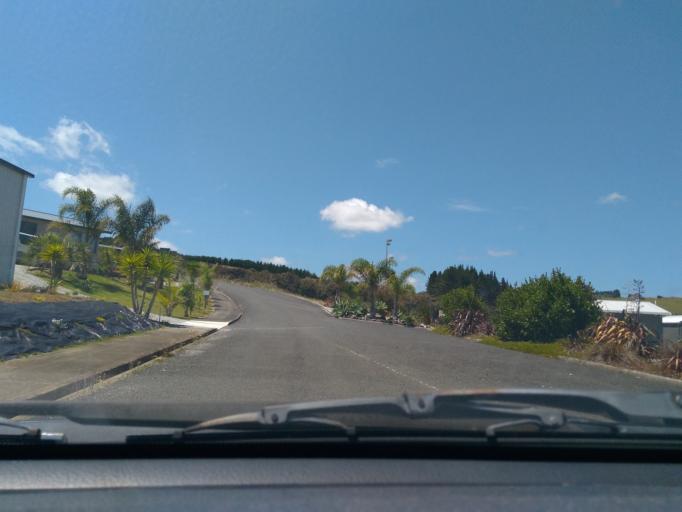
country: NZ
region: Northland
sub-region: Far North District
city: Taipa
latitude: -34.9946
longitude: 173.5049
